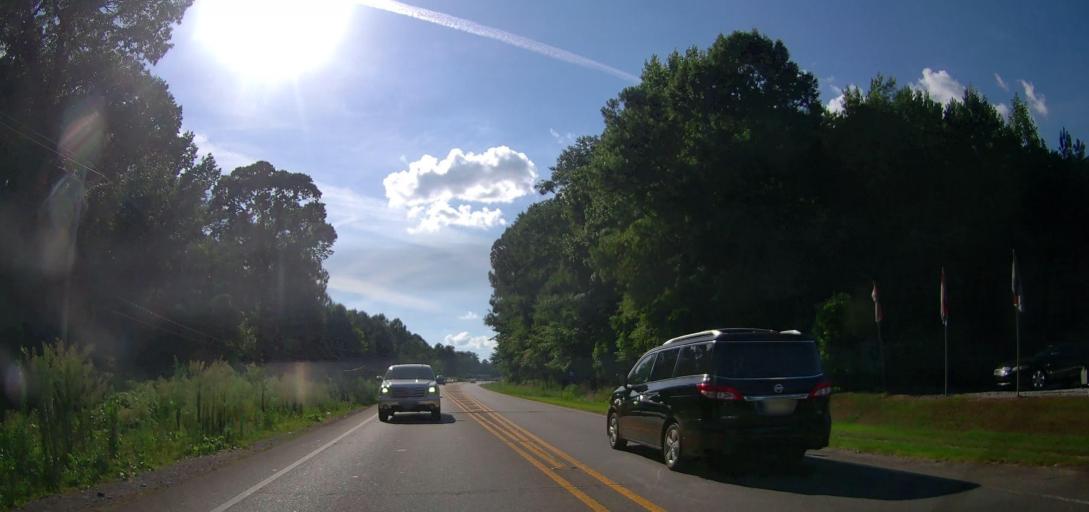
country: US
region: Alabama
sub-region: Tuscaloosa County
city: Holt
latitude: 33.1933
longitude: -87.4710
